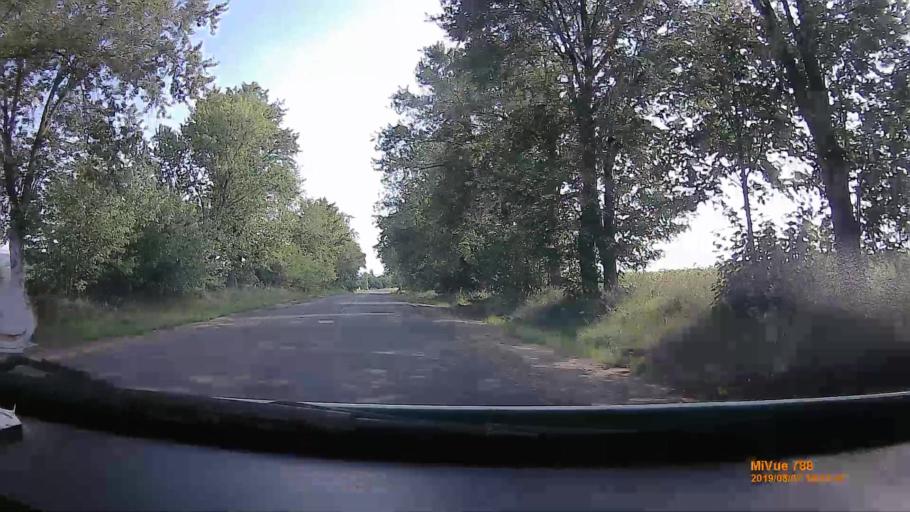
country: HU
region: Borsod-Abauj-Zemplen
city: Abaujszanto
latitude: 48.3518
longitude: 21.2129
